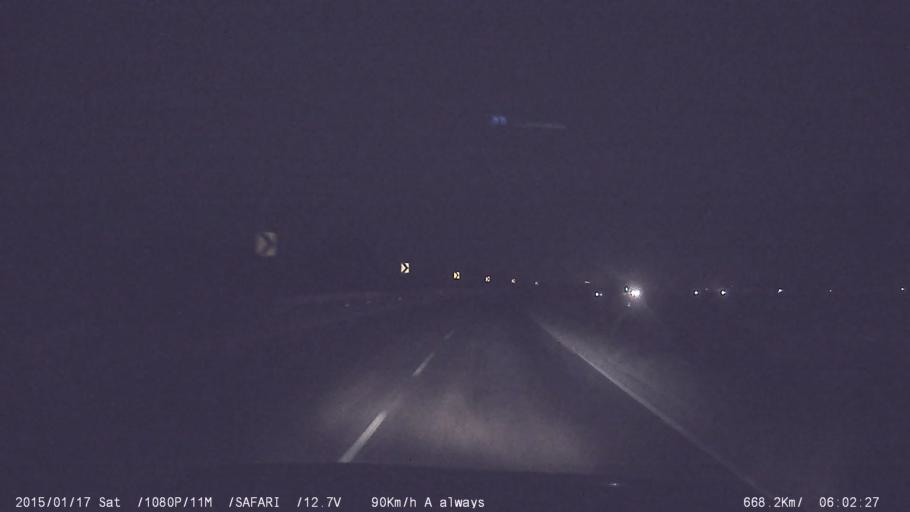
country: IN
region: Tamil Nadu
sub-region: Kancheepuram
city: Kanchipuram
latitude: 12.8906
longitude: 79.5932
